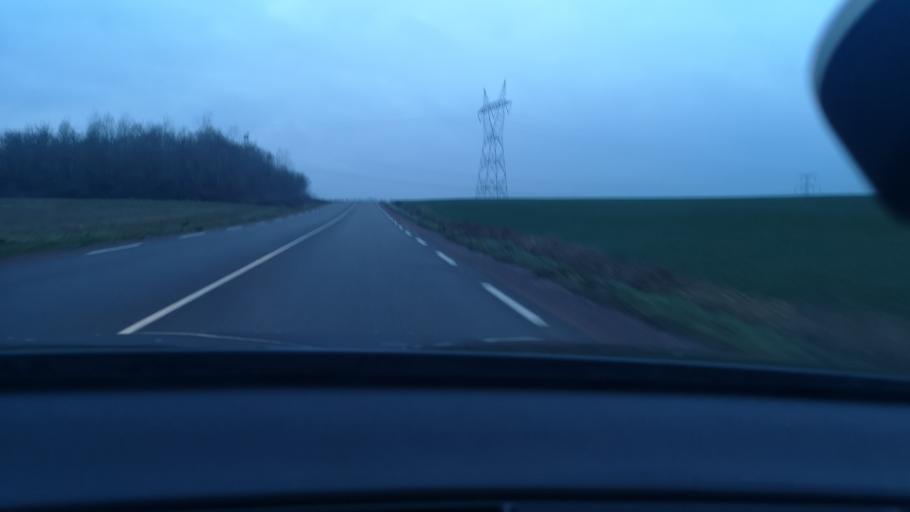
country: FR
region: Bourgogne
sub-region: Departement de Saone-et-Loire
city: Verdun-sur-le-Doubs
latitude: 47.0052
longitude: 5.0114
